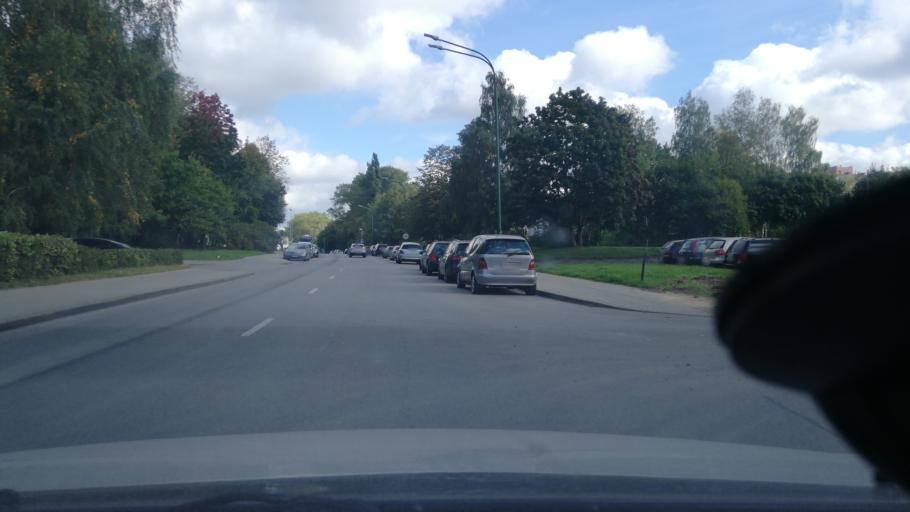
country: LT
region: Klaipedos apskritis
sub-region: Klaipeda
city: Klaipeda
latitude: 55.6815
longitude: 21.1693
